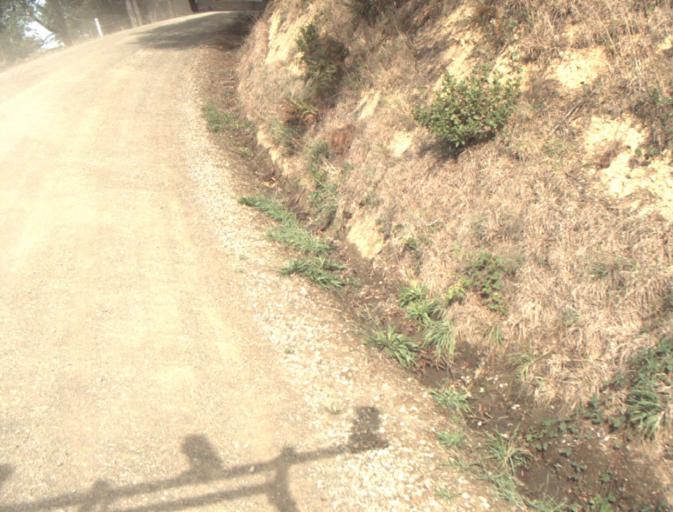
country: AU
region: Tasmania
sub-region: Launceston
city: Mayfield
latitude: -41.1927
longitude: 147.1905
